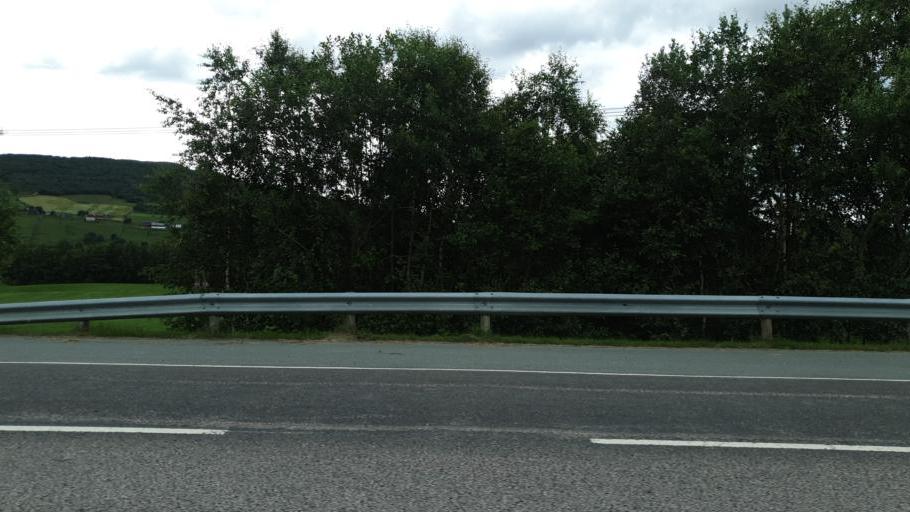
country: NO
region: Sor-Trondelag
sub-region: Oppdal
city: Oppdal
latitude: 62.5760
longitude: 9.6530
